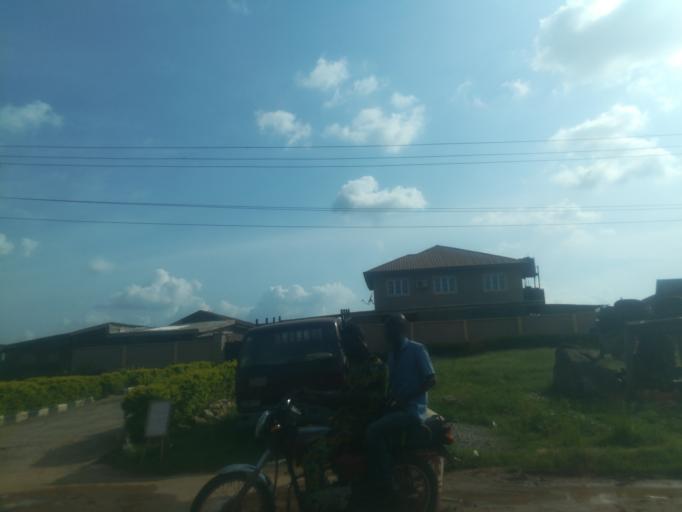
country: NG
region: Oyo
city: Ido
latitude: 7.3995
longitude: 3.8031
